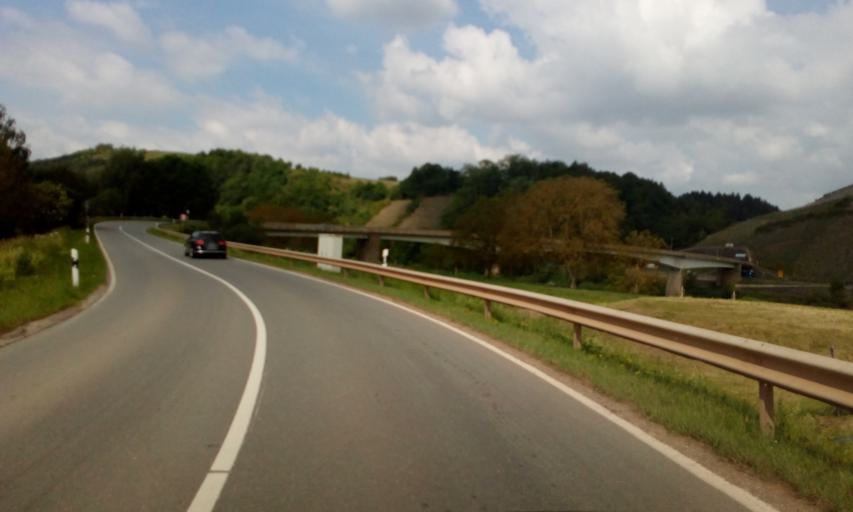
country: DE
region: Rheinland-Pfalz
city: Thornich
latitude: 49.8358
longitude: 6.8398
